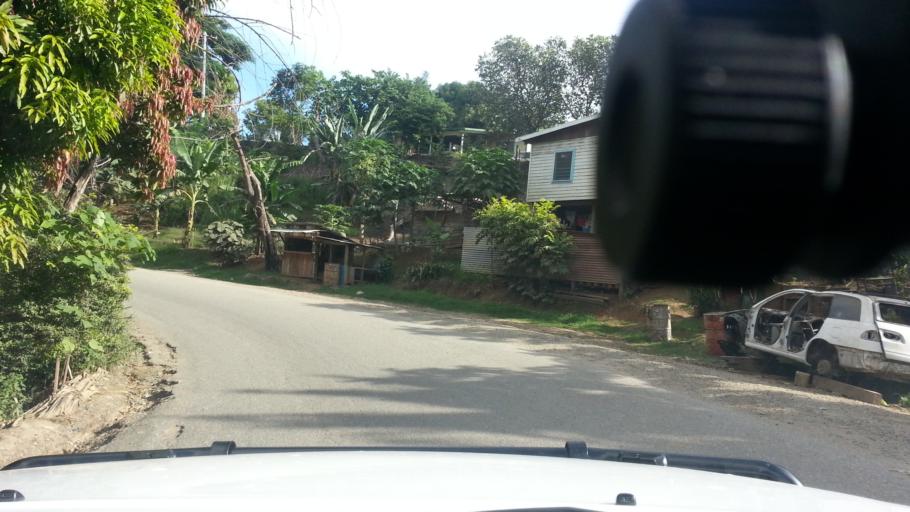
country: SB
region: Guadalcanal
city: Honiara
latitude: -9.4481
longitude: 159.9825
